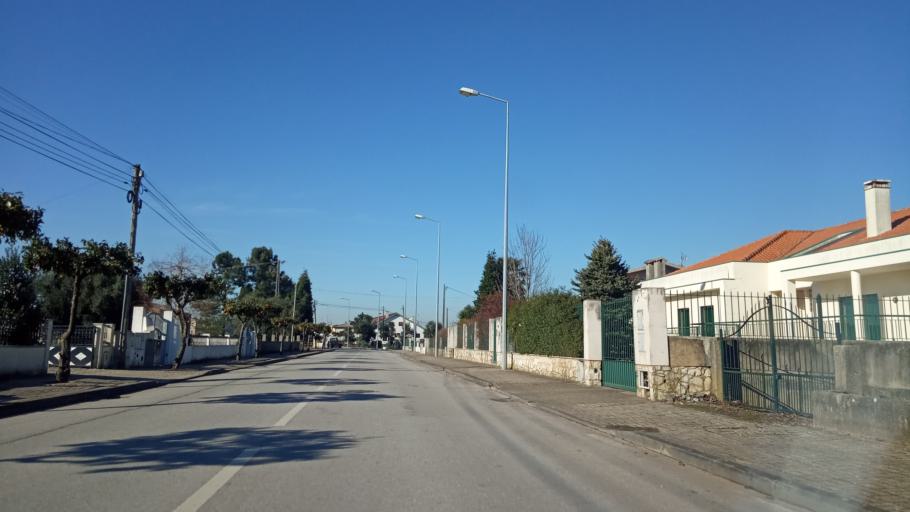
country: PT
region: Aveiro
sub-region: Anadia
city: Anadia
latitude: 40.4320
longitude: -8.4258
